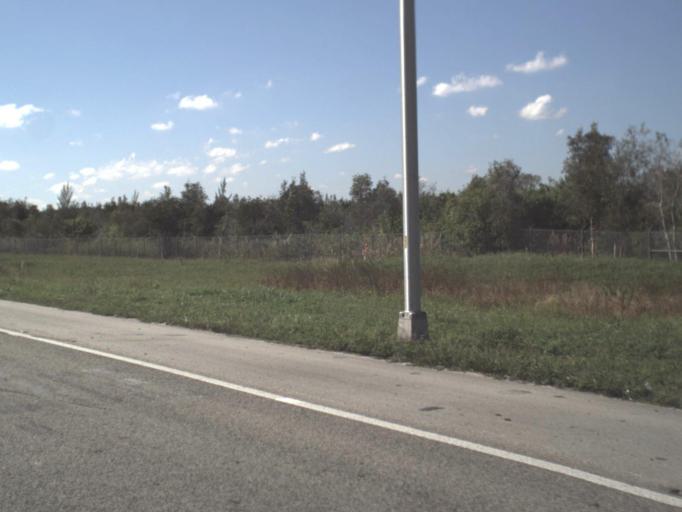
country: US
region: Florida
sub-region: Miami-Dade County
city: Doral
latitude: 25.8323
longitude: -80.3872
